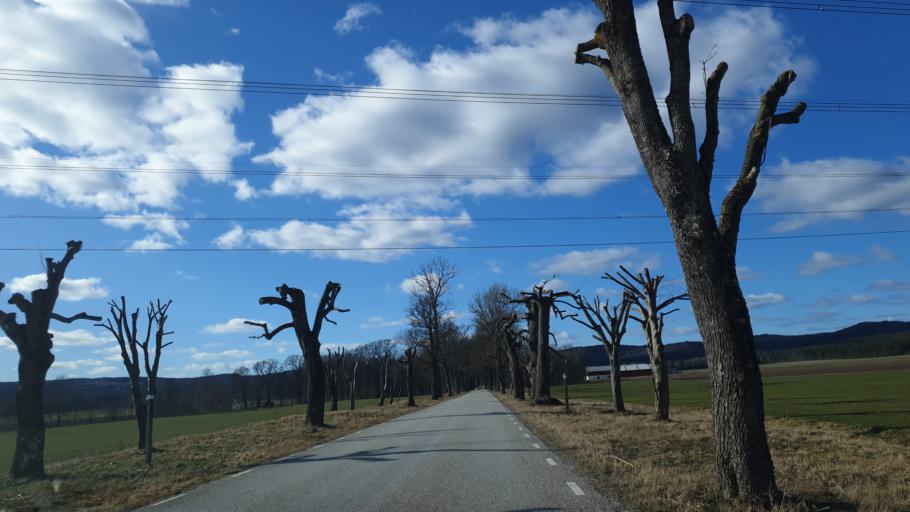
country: SE
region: OErebro
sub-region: Orebro Kommun
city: Garphyttan
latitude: 59.3404
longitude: 15.0230
